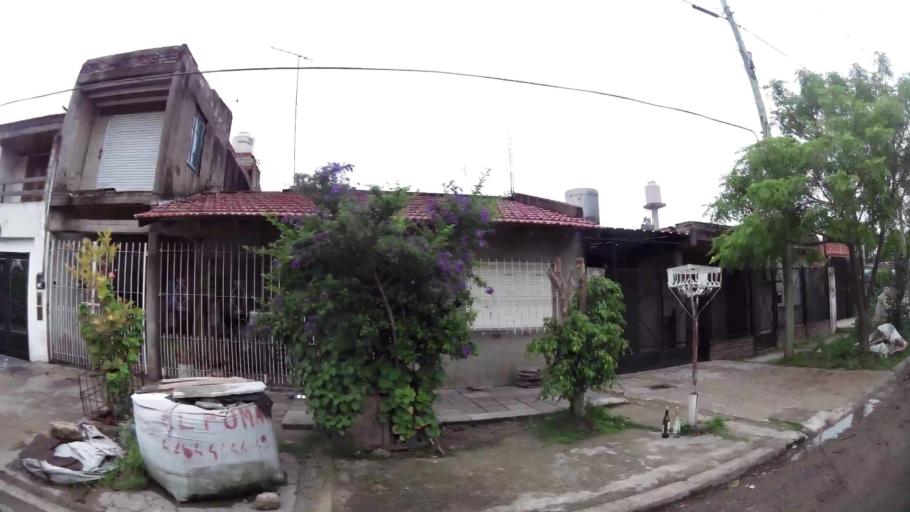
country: AR
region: Buenos Aires
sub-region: Partido de Lanus
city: Lanus
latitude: -34.7374
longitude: -58.3591
